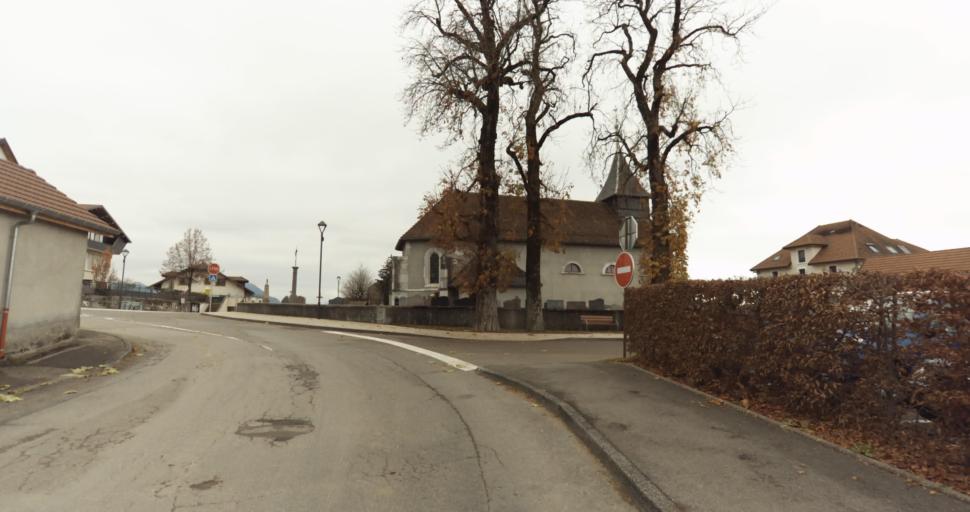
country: FR
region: Rhone-Alpes
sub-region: Departement de la Haute-Savoie
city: Villaz
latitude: 45.9790
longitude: 6.1820
